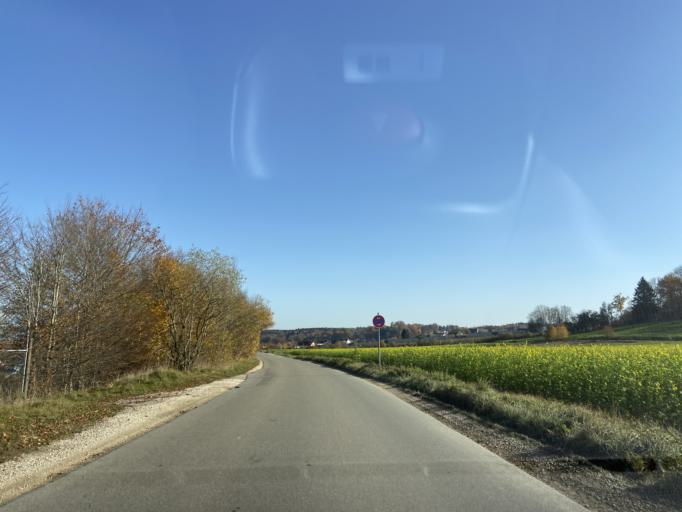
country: DE
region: Baden-Wuerttemberg
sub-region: Tuebingen Region
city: Krauchenwies
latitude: 48.0308
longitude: 9.2849
